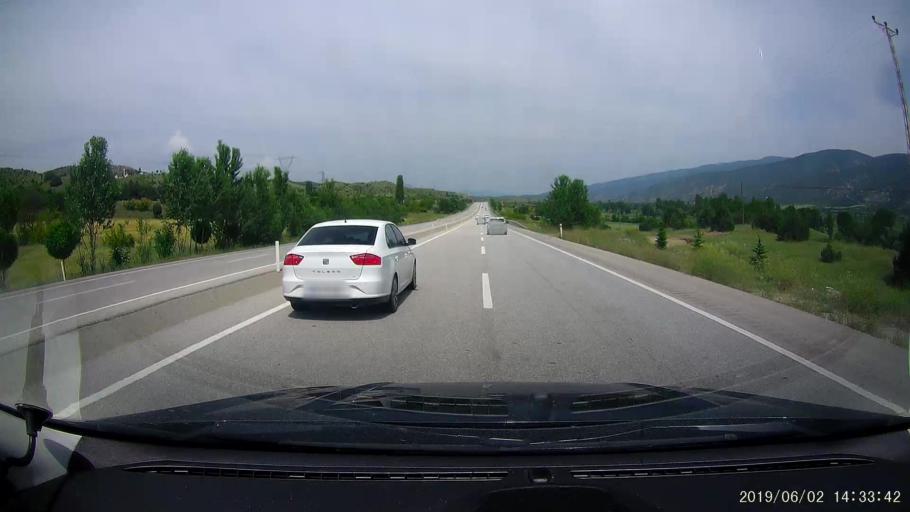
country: TR
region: Kastamonu
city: Tosya
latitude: 41.0331
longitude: 34.1761
